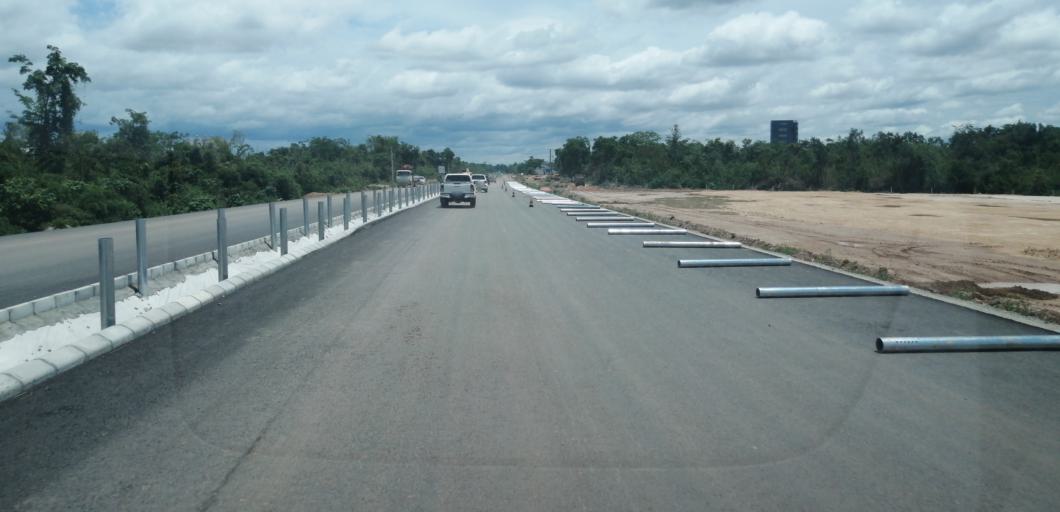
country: LA
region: Vientiane
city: Muang Phon-Hong
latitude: 18.2939
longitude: 102.4577
